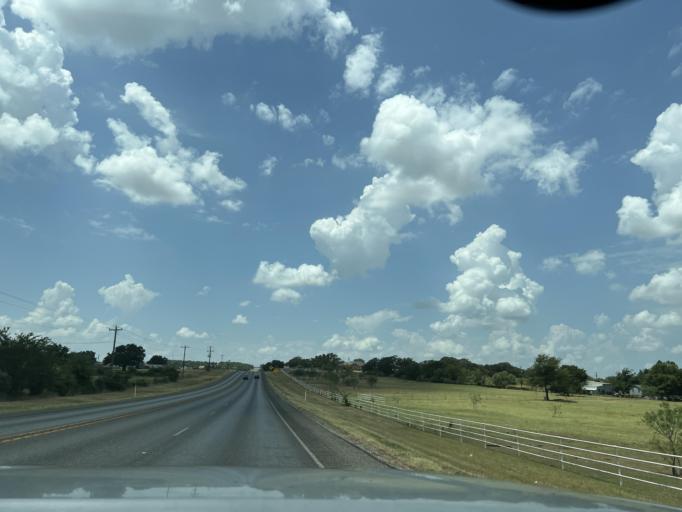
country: US
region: Texas
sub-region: Parker County
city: Springtown
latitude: 32.9463
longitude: -97.6915
